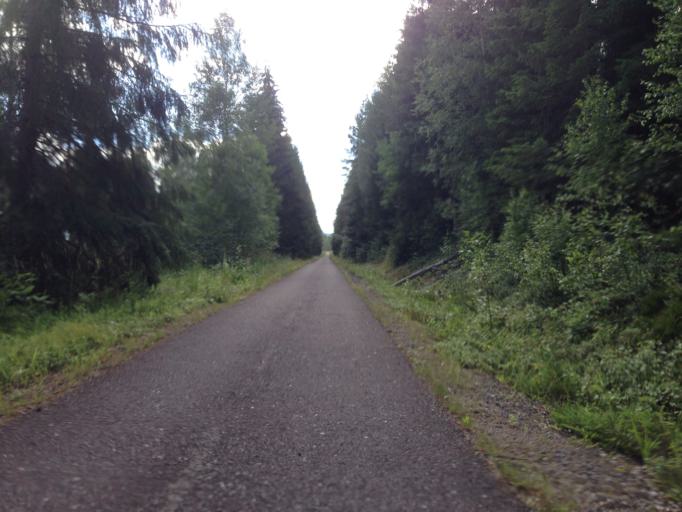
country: SE
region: Dalarna
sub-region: Ludvika Kommun
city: Ludvika
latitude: 60.2036
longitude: 15.1023
